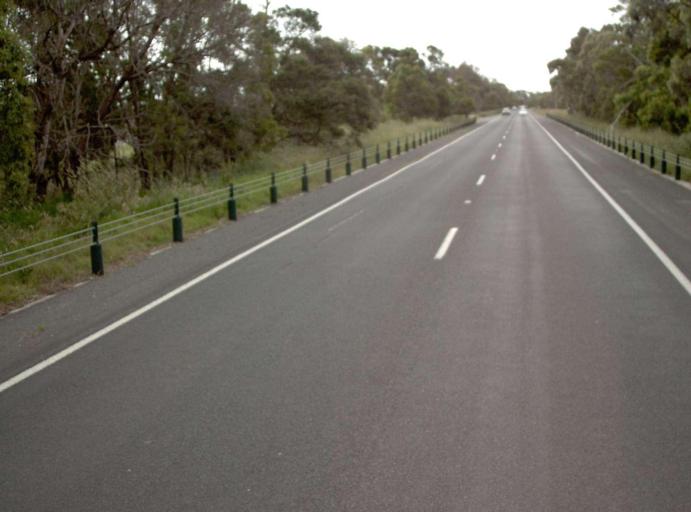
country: AU
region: Victoria
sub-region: Casey
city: Tooradin
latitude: -38.2036
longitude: 145.3638
